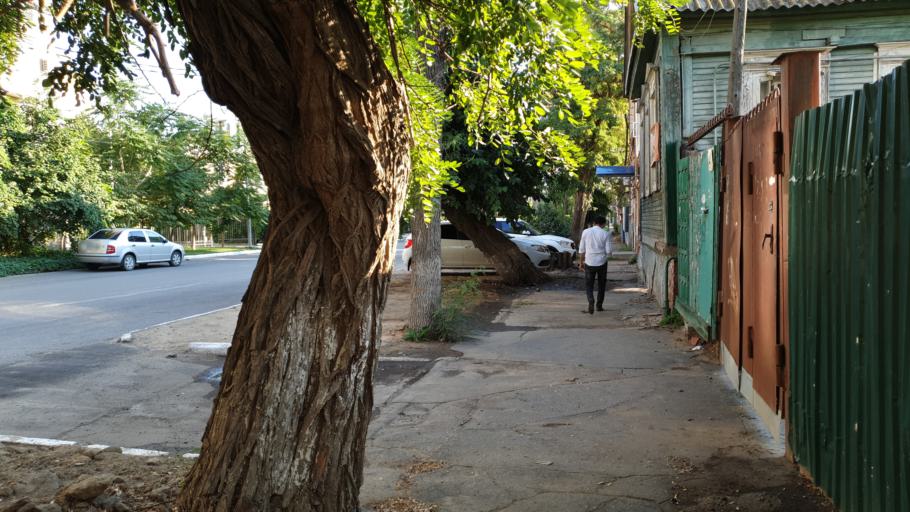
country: RU
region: Astrakhan
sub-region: Gorod Astrakhan'
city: Astrakhan'
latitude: 46.3496
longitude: 48.0249
